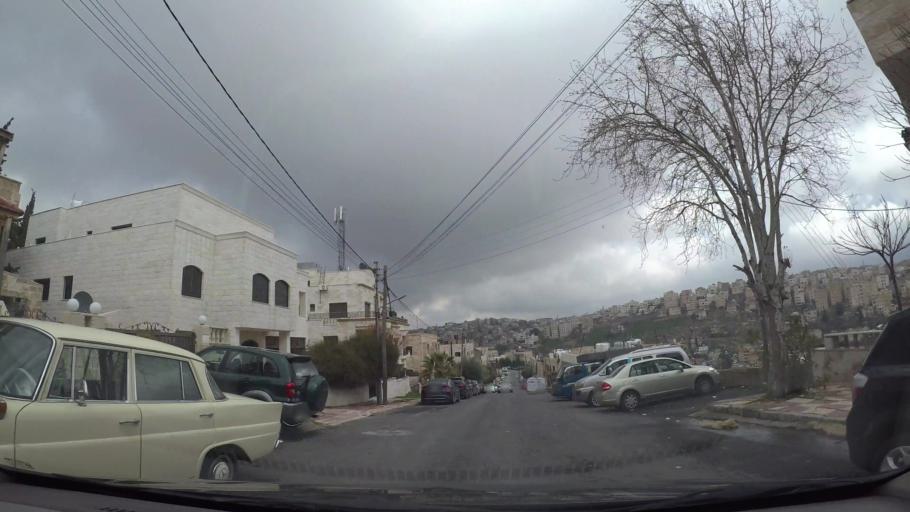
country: JO
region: Amman
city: Amman
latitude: 31.9414
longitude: 35.9024
